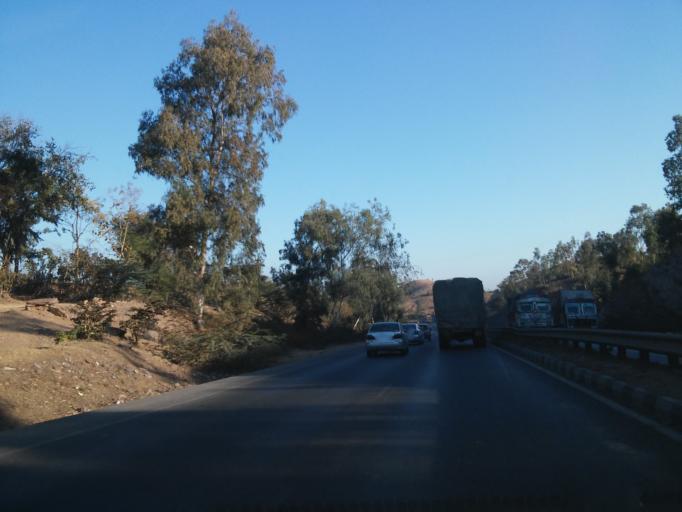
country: IN
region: Rajasthan
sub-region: Dungarpur
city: Dungarpur
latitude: 23.9030
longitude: 73.5464
